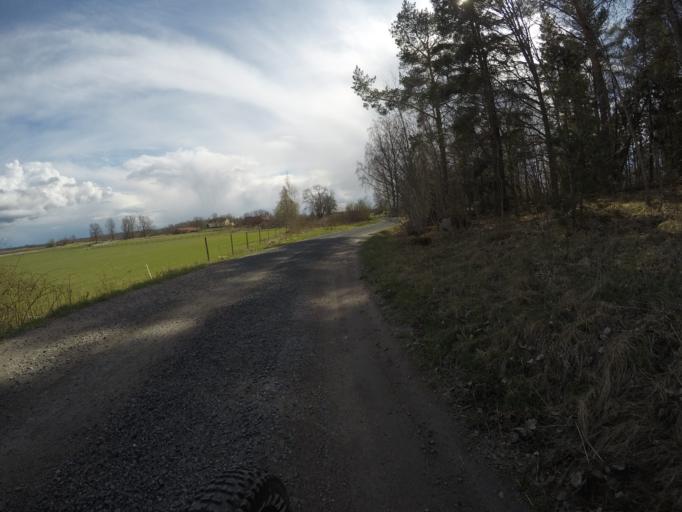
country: SE
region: Vaestmanland
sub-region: Kungsors Kommun
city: Kungsoer
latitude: 59.2845
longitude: 16.1514
